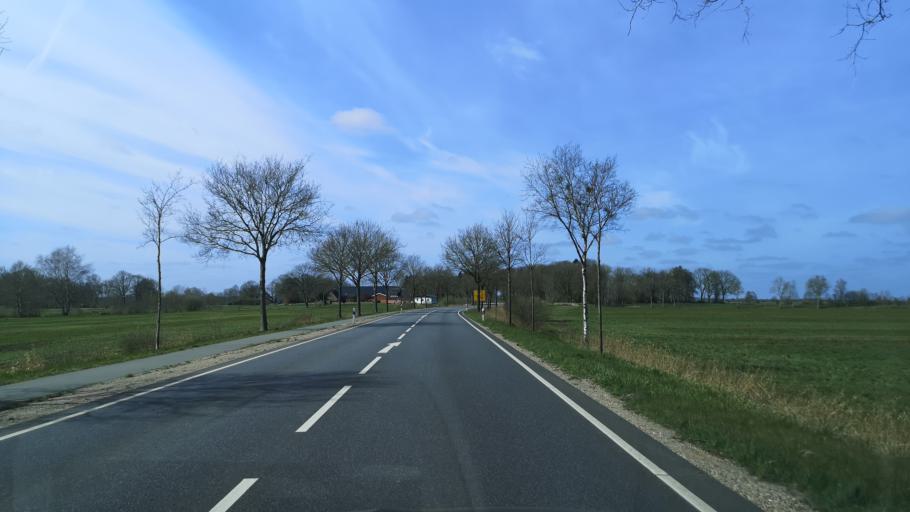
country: DE
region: Schleswig-Holstein
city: Prinzenmoor
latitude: 54.2221
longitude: 9.4606
